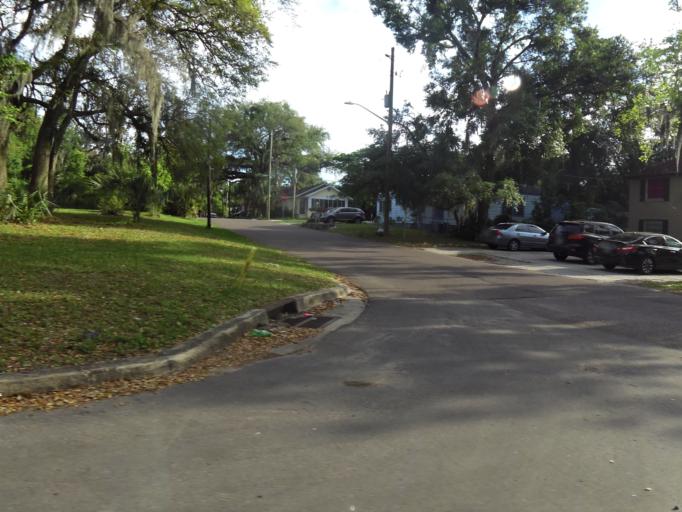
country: US
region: Florida
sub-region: Duval County
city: Jacksonville
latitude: 30.3649
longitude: -81.6553
